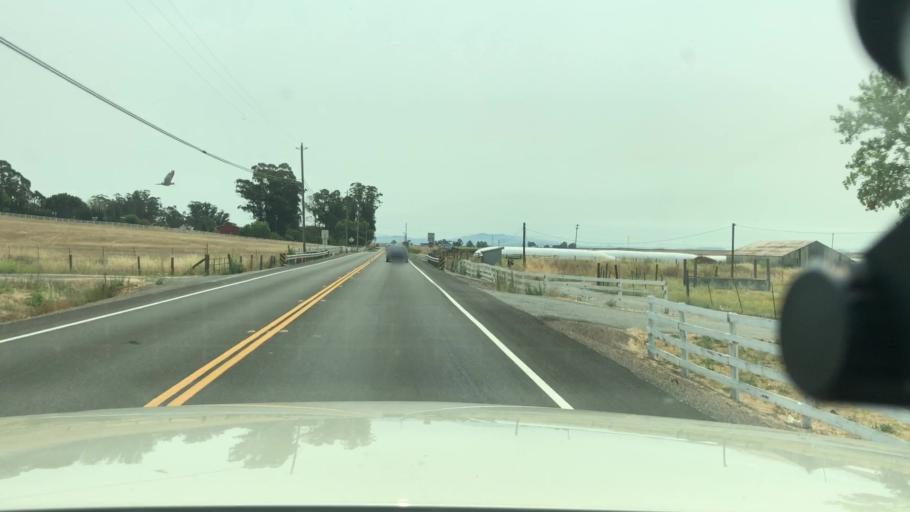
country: US
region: California
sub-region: Marin County
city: Black Point-Green Point
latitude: 38.1573
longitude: -122.4981
